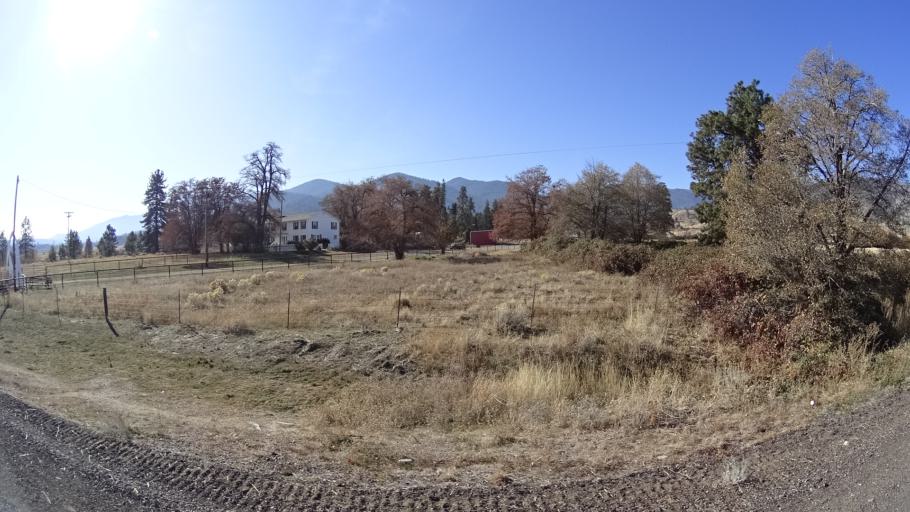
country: US
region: California
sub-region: Siskiyou County
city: Weed
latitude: 41.4484
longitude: -122.4509
